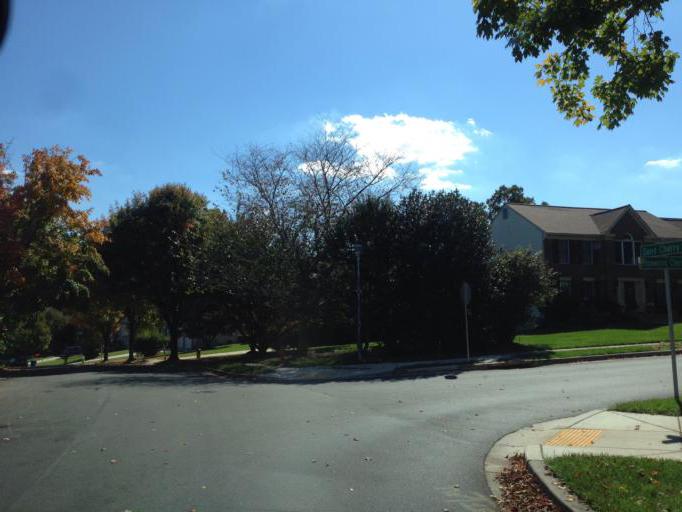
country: US
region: Maryland
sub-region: Howard County
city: Fulton
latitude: 39.1382
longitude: -76.8995
